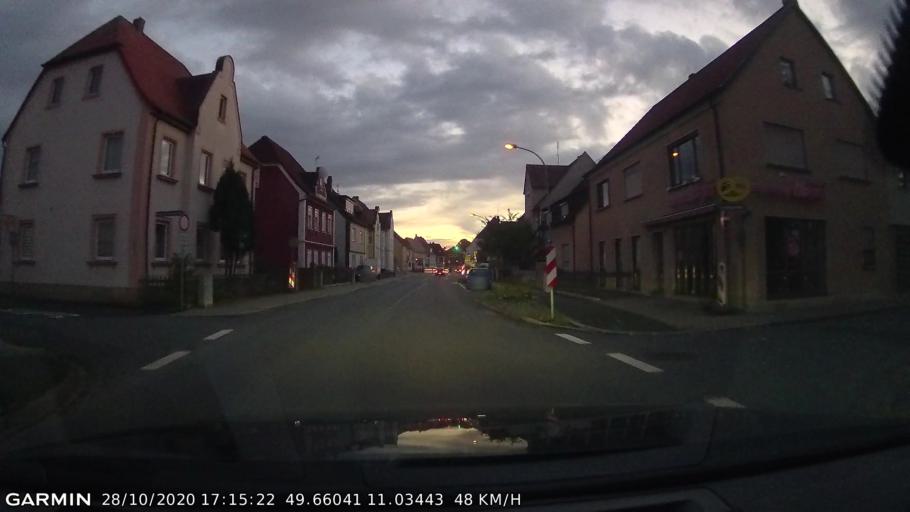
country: DE
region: Bavaria
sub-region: Regierungsbezirk Mittelfranken
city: Baiersdorf
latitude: 49.6603
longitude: 11.0344
